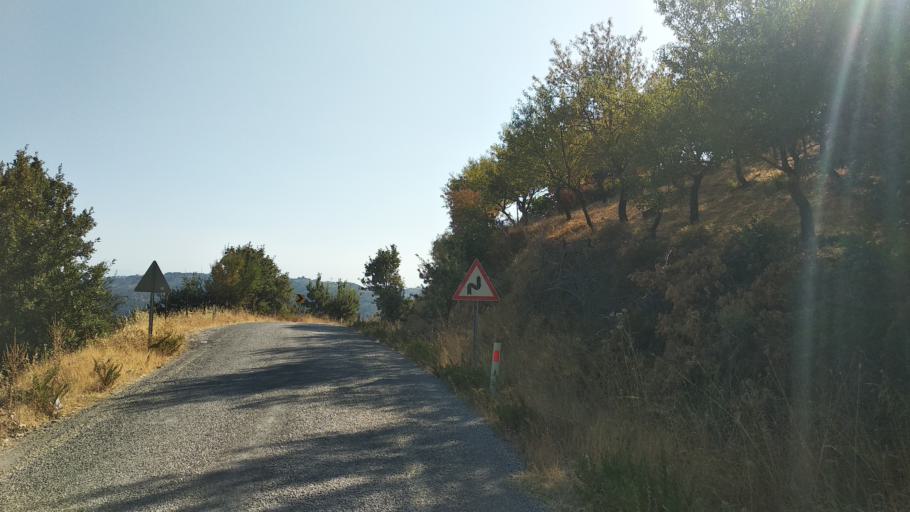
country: TR
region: Izmir
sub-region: Seferihisar
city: Seferhisar
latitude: 38.3223
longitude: 26.9360
